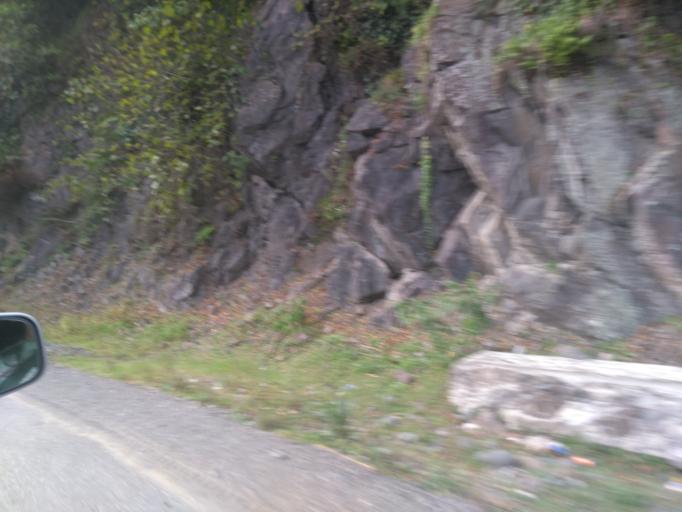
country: TR
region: Artvin
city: Muratli
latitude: 41.5475
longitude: 41.7559
